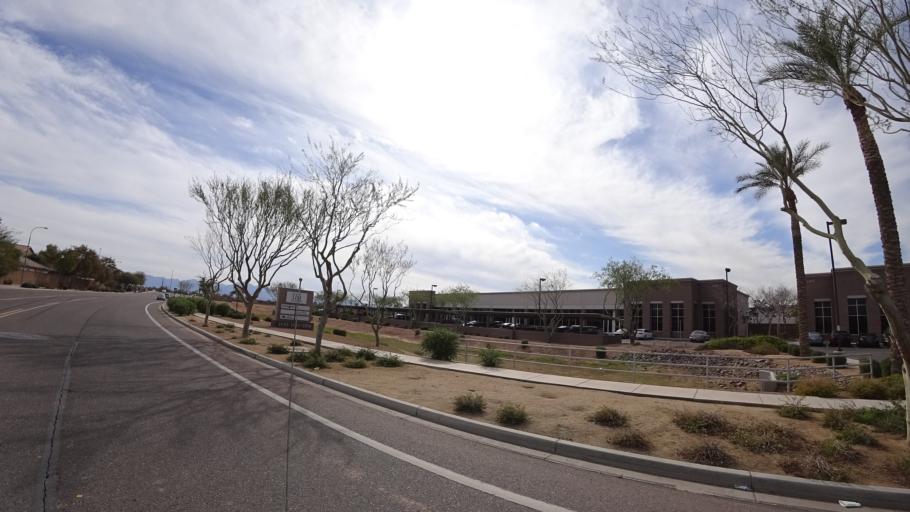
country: US
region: Arizona
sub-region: Maricopa County
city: Tolleson
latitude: 33.4674
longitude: -112.2641
